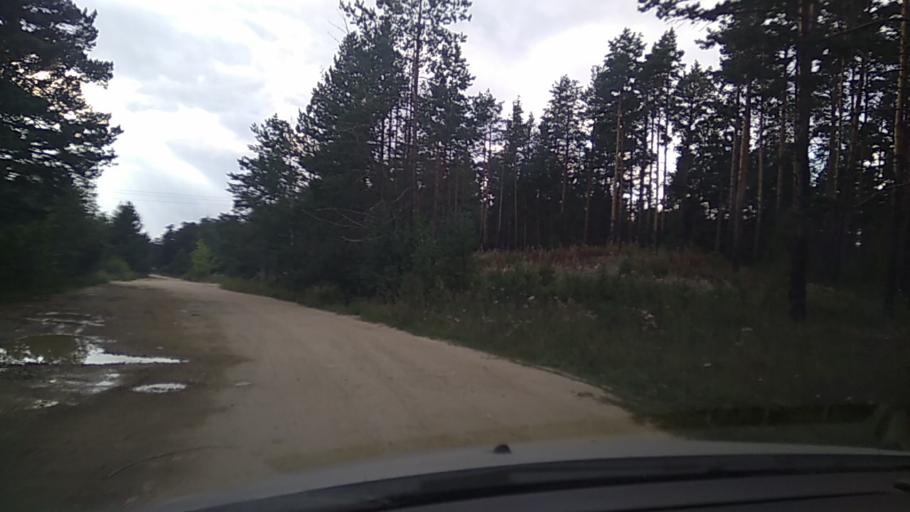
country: RU
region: Chelyabinsk
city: Kyshtym
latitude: 55.6858
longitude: 60.5672
